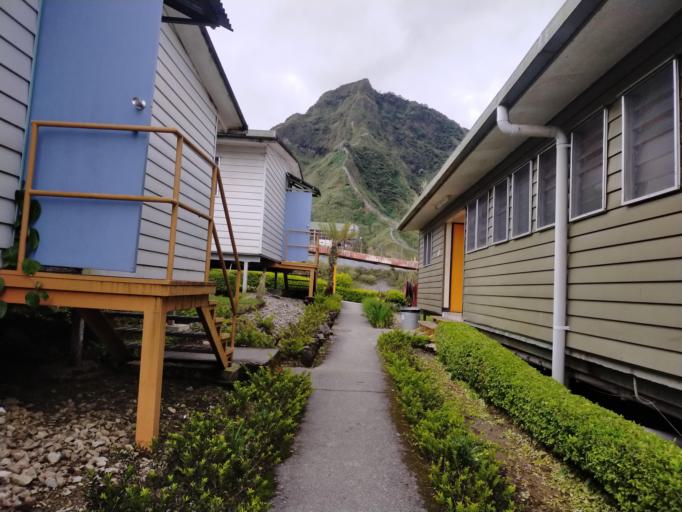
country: PG
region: Enga
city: Porgera
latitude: -5.4622
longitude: 143.1043
